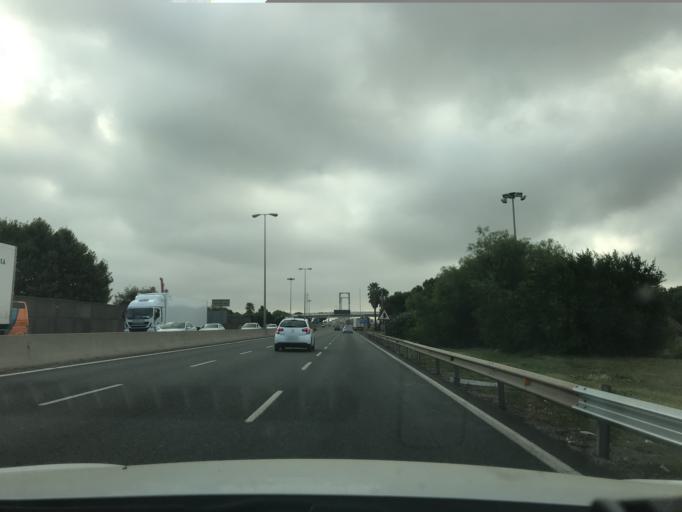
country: ES
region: Andalusia
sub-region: Provincia de Sevilla
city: San Juan de Aznalfarache
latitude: 37.3608
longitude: -6.0073
